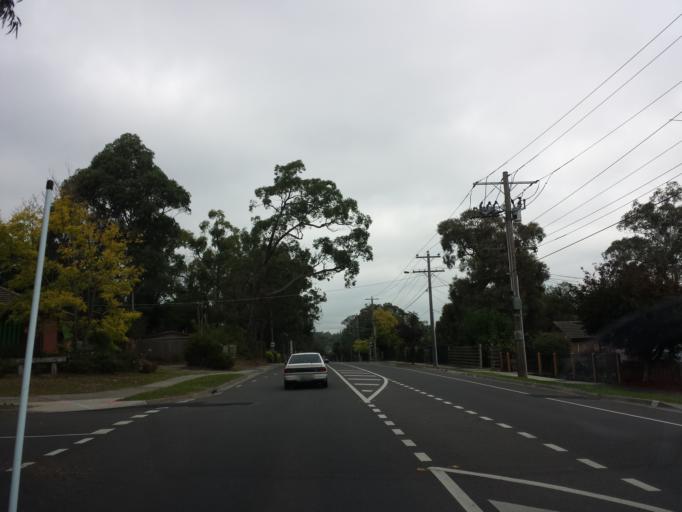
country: AU
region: Victoria
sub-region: Knox
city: The Basin
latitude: -37.8485
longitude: 145.2992
